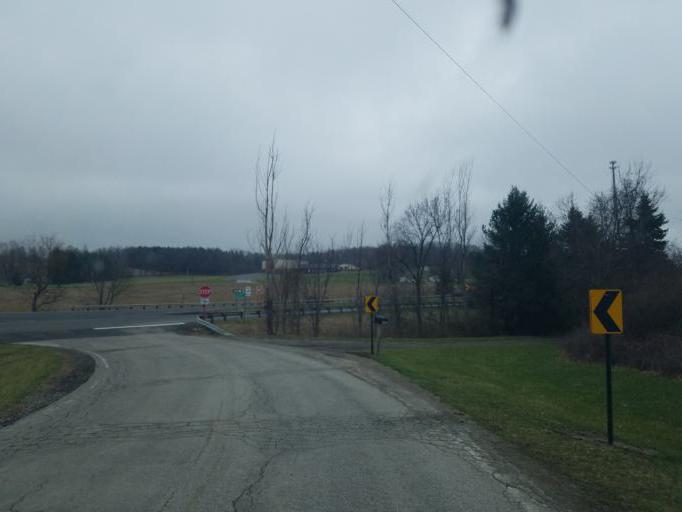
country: US
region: Ohio
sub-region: Sandusky County
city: Bellville
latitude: 40.6784
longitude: -82.5209
